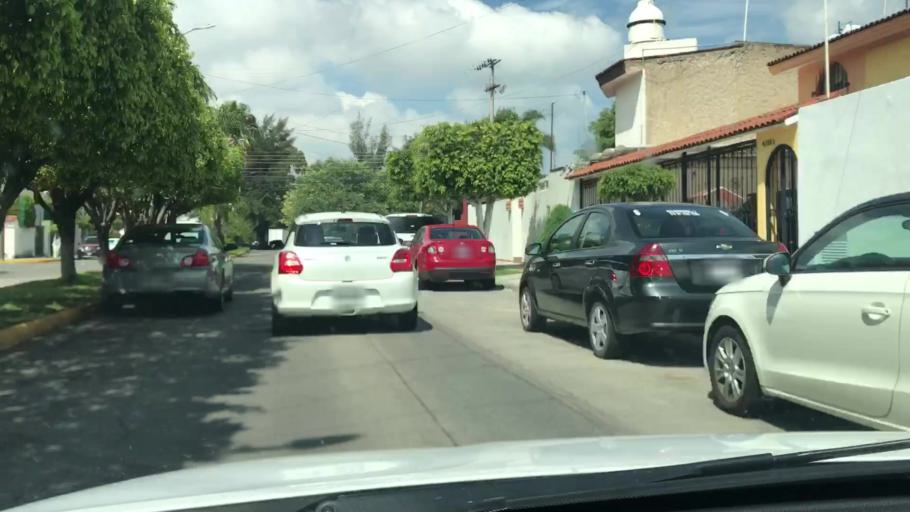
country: MX
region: Jalisco
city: Guadalajara
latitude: 20.6606
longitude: -103.4139
